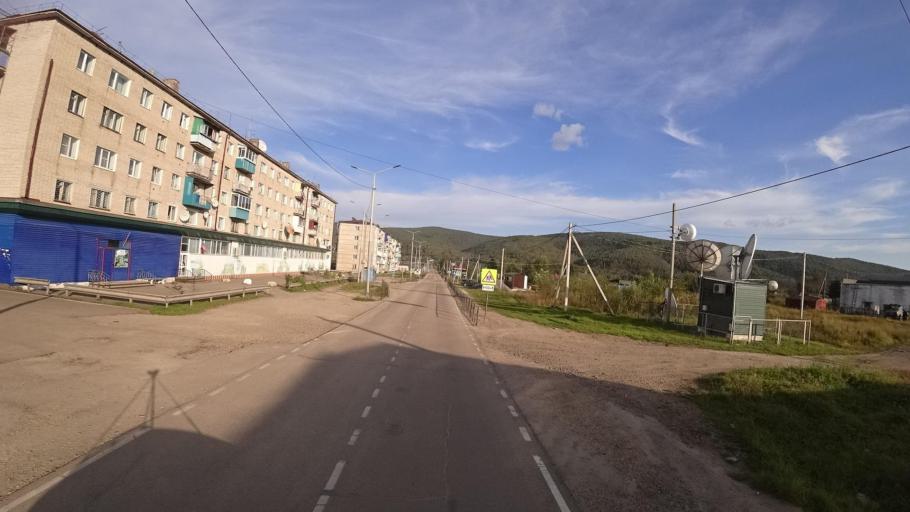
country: RU
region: Jewish Autonomous Oblast
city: Kul'dur
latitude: 49.2020
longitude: 131.6243
